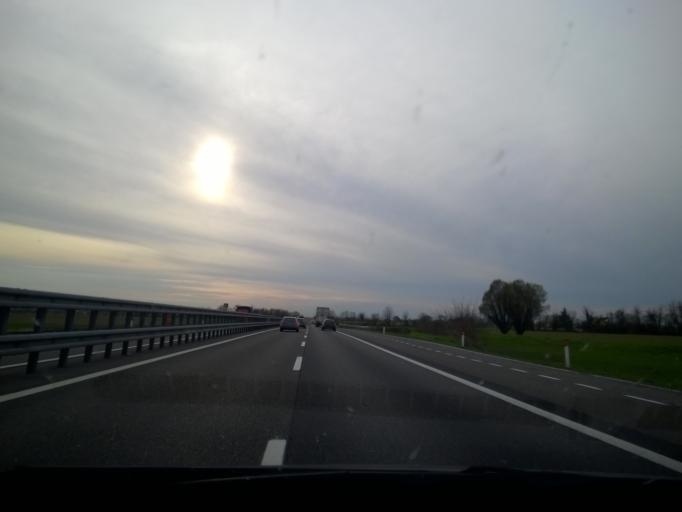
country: IT
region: Emilia-Romagna
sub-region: Provincia di Piacenza
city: San Nicolo
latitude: 45.0643
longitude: 9.5870
